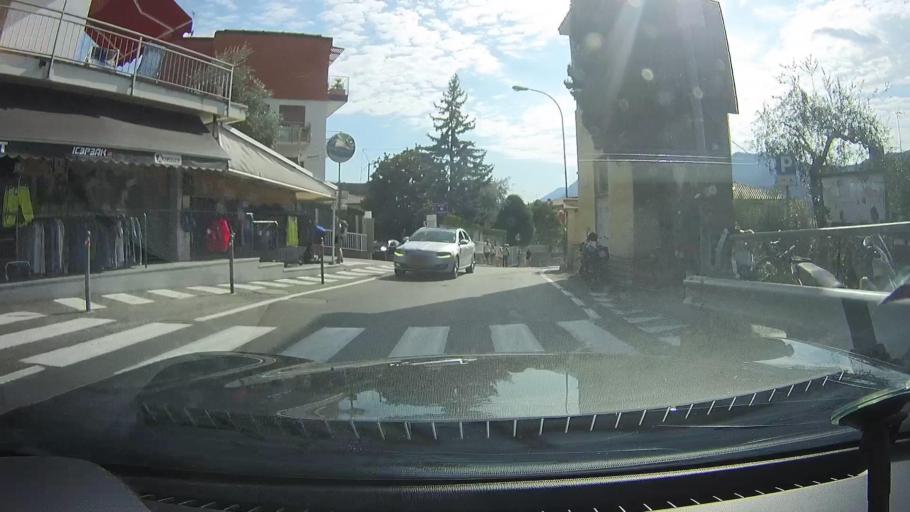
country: IT
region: Veneto
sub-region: Provincia di Verona
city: Malcesine
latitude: 45.7659
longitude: 10.8124
